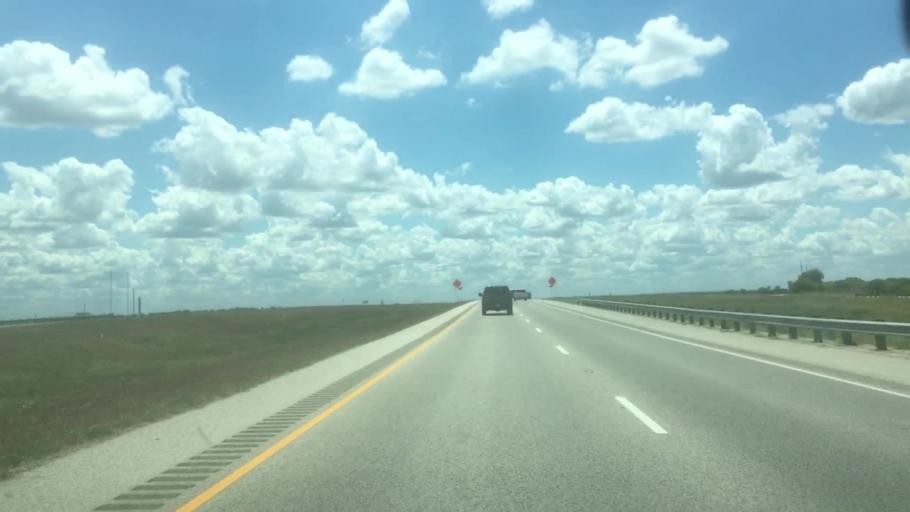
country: US
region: Texas
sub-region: Caldwell County
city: Martindale
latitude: 29.7999
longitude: -97.7788
